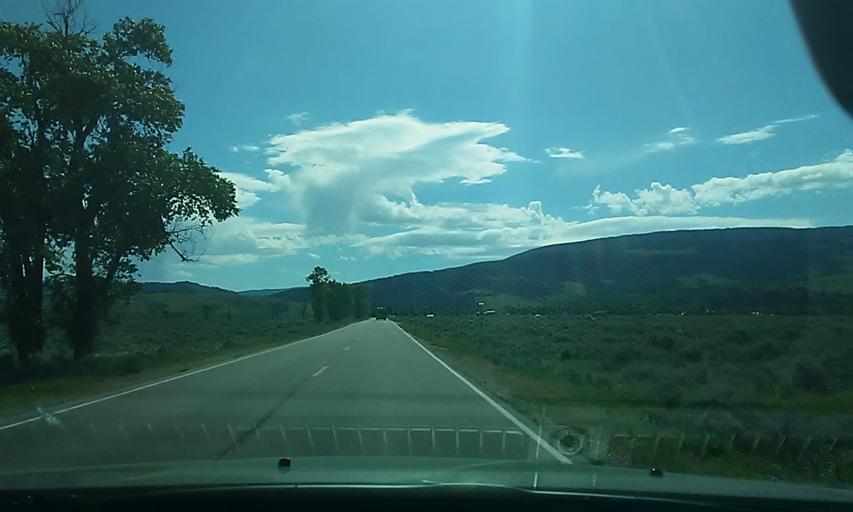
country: US
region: Wyoming
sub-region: Teton County
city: Jackson
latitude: 43.6251
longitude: -110.6405
